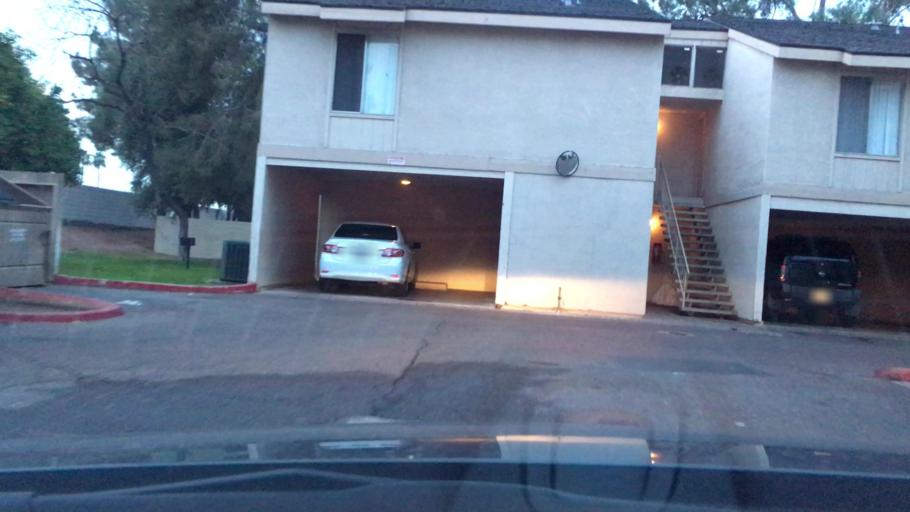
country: US
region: Arizona
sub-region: Maricopa County
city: Tempe
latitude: 33.3775
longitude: -111.9115
